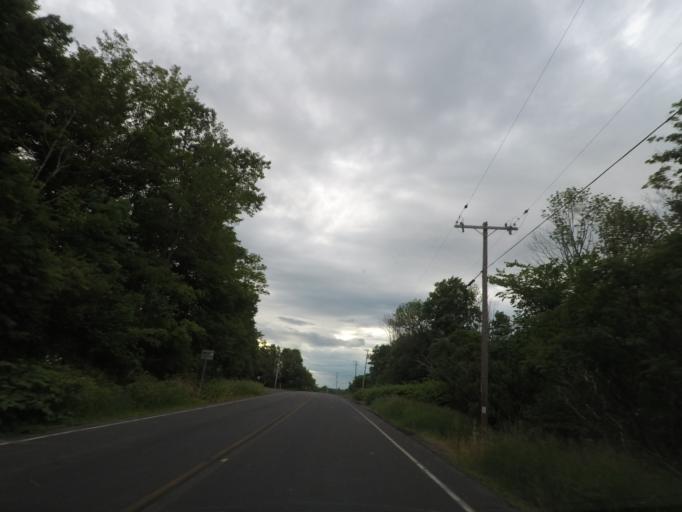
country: US
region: New York
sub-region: Dutchess County
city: Pine Plains
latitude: 41.9687
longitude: -73.5553
